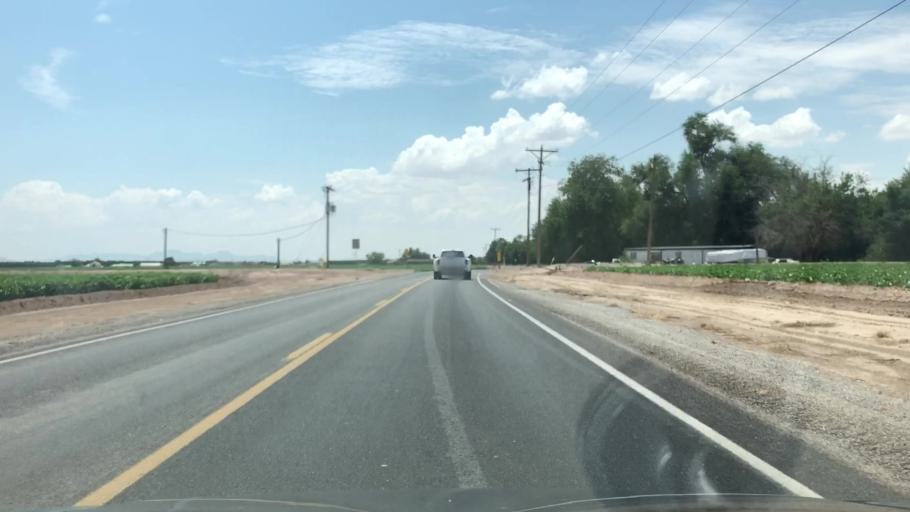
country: US
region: New Mexico
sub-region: Dona Ana County
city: La Union
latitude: 31.9749
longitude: -106.6516
